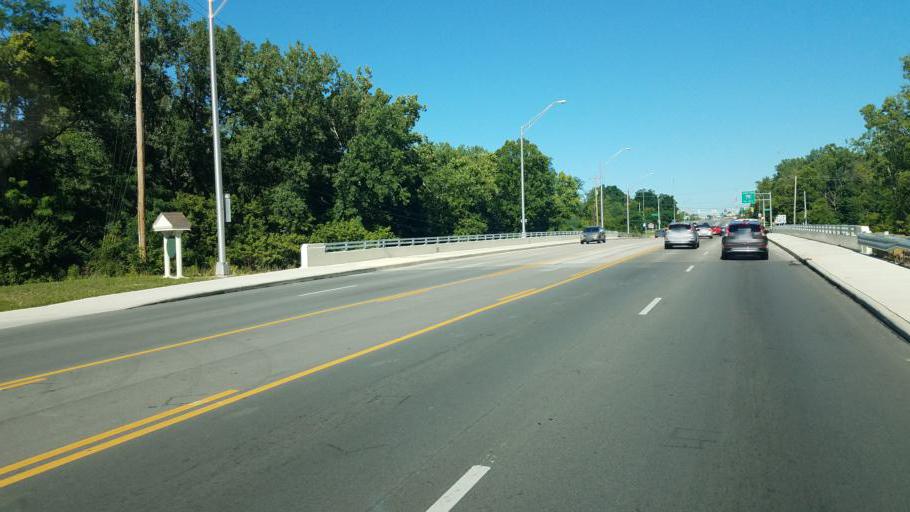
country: US
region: Ohio
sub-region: Franklin County
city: Whitehall
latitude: 39.9547
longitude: -82.8540
